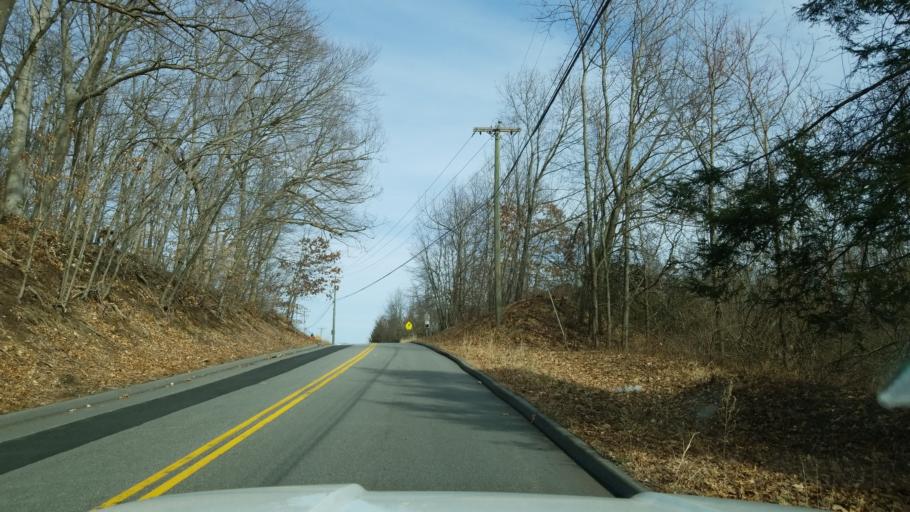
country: US
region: Connecticut
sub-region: Middlesex County
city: Cromwell
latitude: 41.6383
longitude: -72.6184
